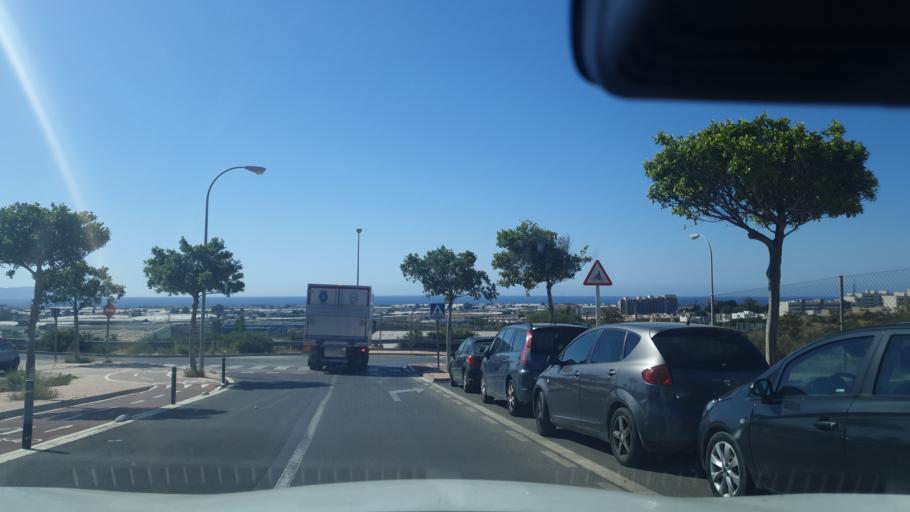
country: ES
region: Andalusia
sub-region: Provincia de Almeria
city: Huercal de Almeria
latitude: 36.8612
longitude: -2.4384
